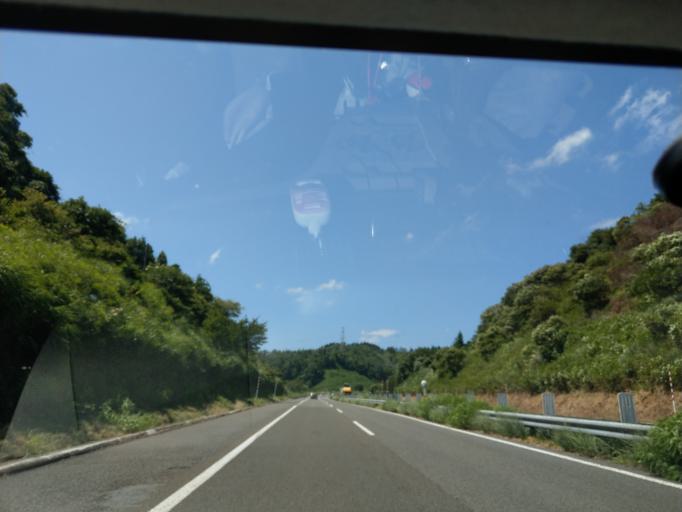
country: JP
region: Akita
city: Omagari
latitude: 39.5699
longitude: 140.3039
